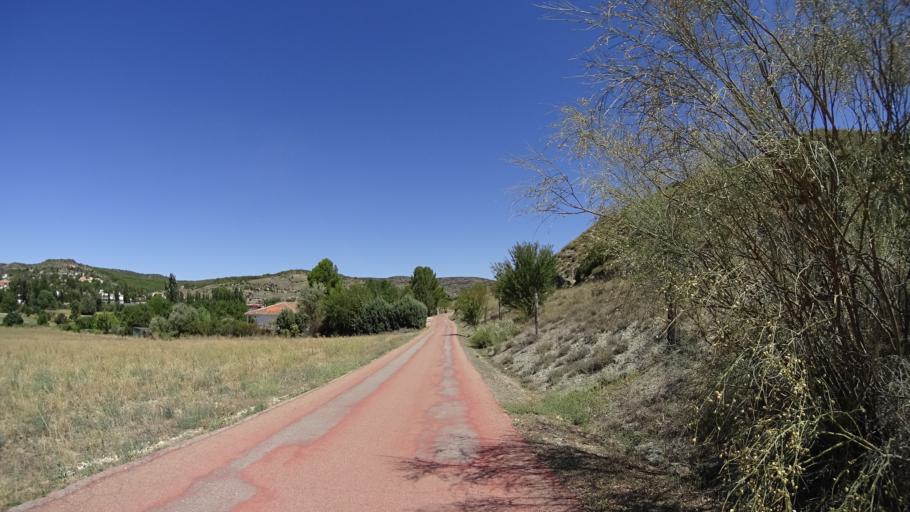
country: ES
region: Madrid
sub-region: Provincia de Madrid
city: Carabana
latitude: 40.2555
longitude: -3.2260
